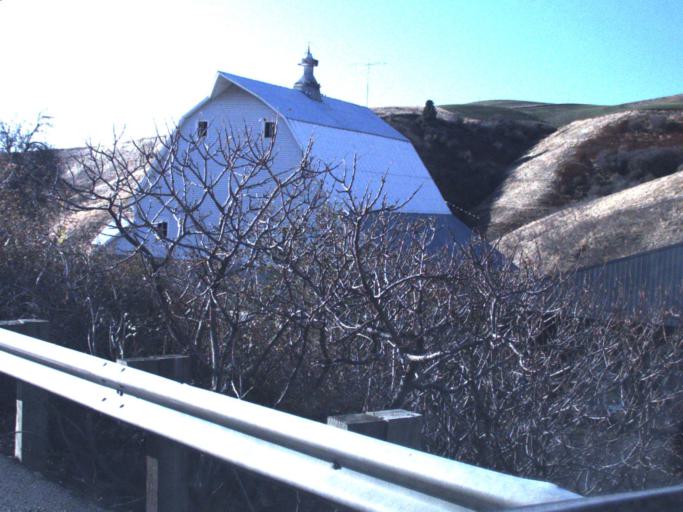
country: US
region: Washington
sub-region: Whitman County
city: Colfax
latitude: 46.7258
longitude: -117.4880
